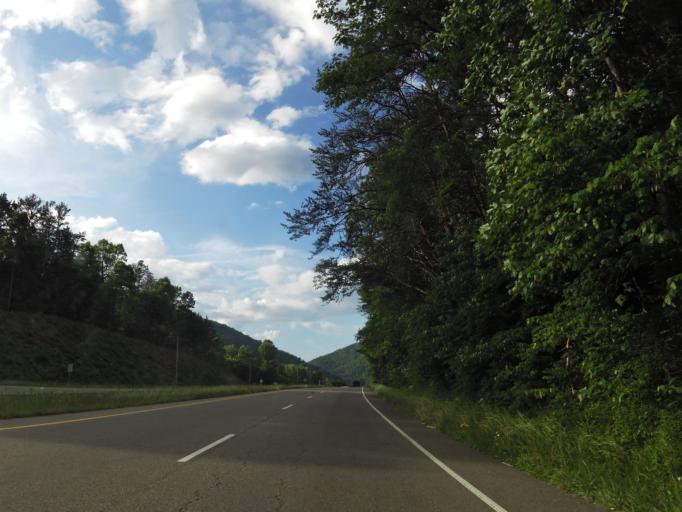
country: US
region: Tennessee
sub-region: Blount County
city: Wildwood
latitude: 35.7157
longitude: -83.8204
